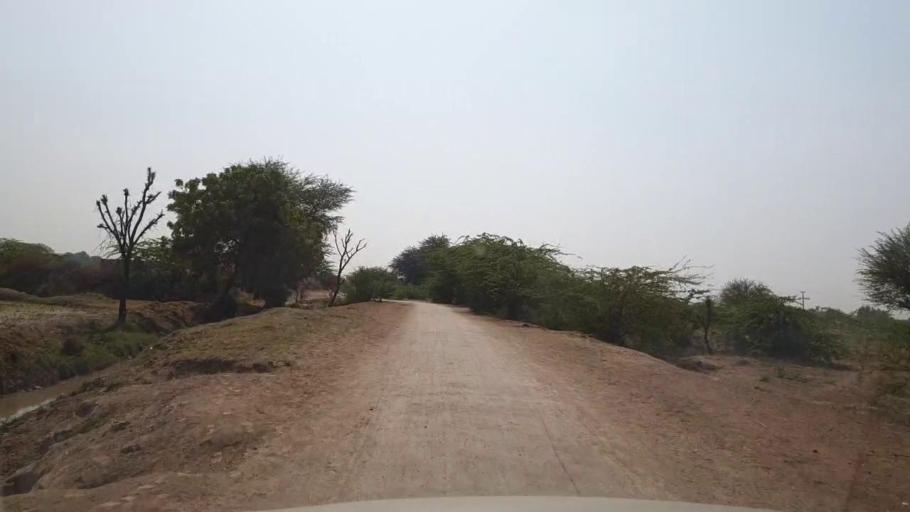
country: PK
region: Sindh
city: Dhoro Naro
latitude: 25.4784
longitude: 69.6401
